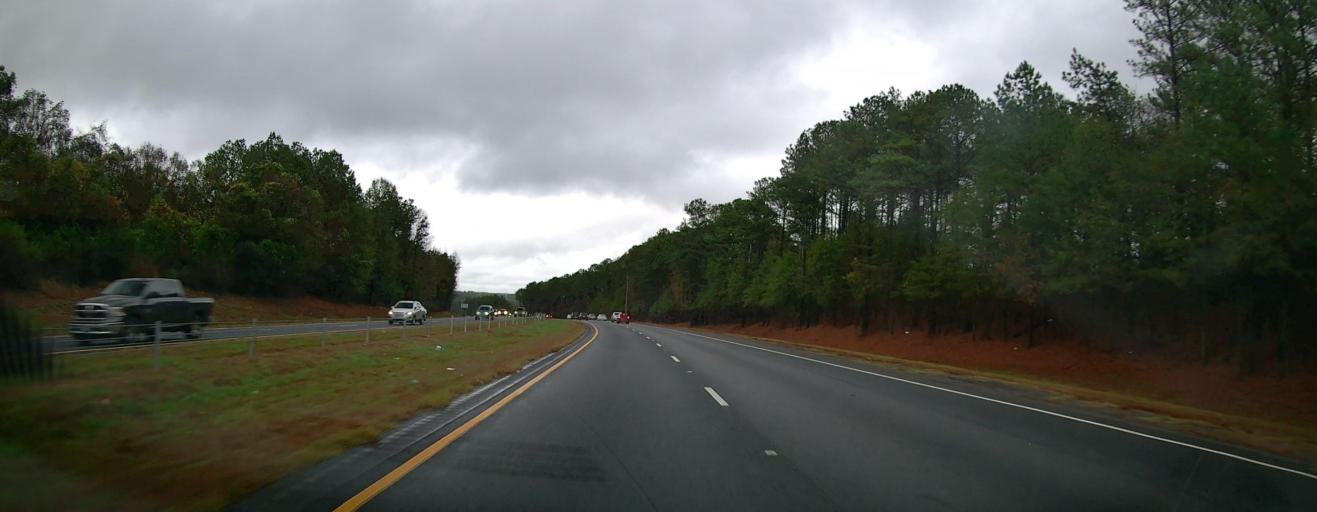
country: US
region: Georgia
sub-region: Clarke County
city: Athens
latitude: 33.9239
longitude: -83.3730
